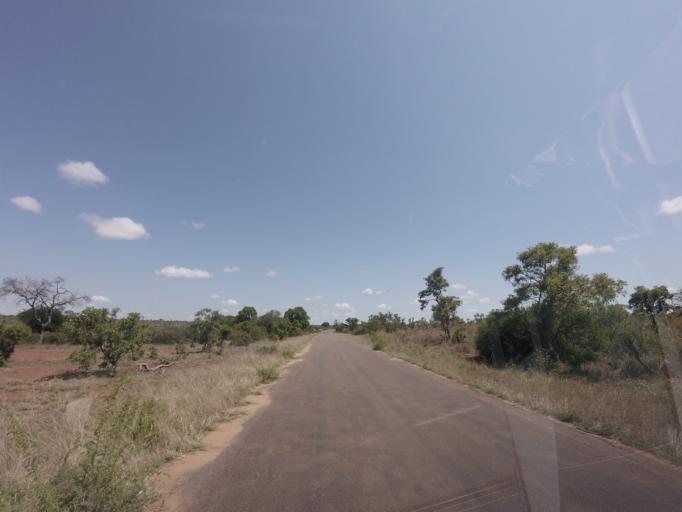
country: ZA
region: Mpumalanga
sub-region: Ehlanzeni District
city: Komatipoort
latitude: -24.9803
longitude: 31.9050
